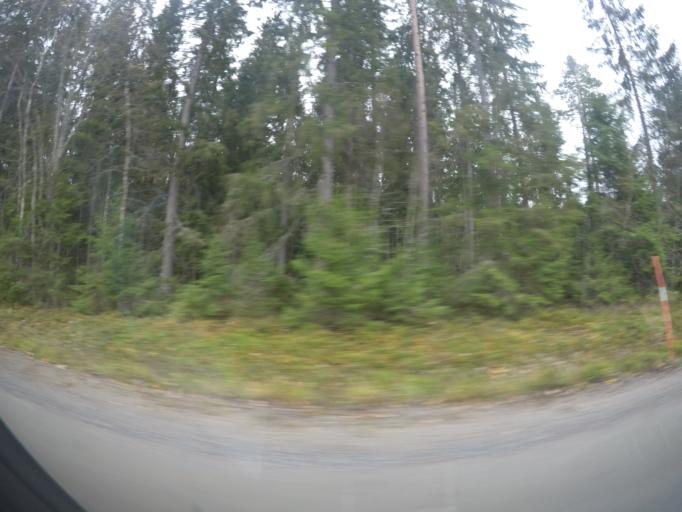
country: SE
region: Vaestmanland
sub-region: Surahammars Kommun
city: Ramnas
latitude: 59.7231
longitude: 16.0935
